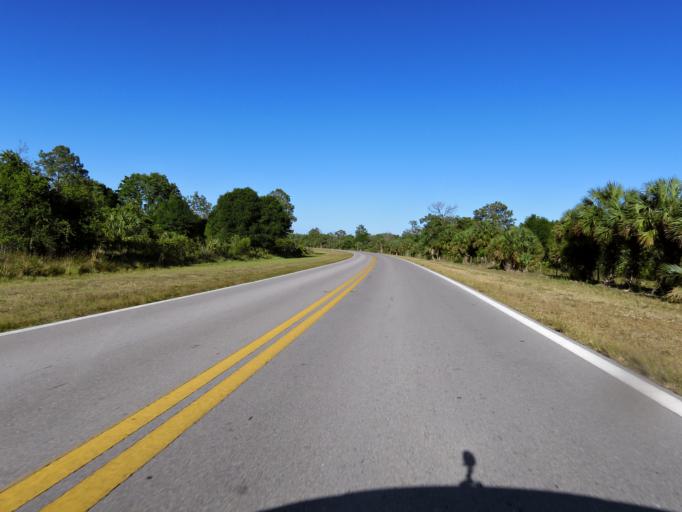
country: US
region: Florida
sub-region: Collier County
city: Immokalee
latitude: 26.2955
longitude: -81.3665
